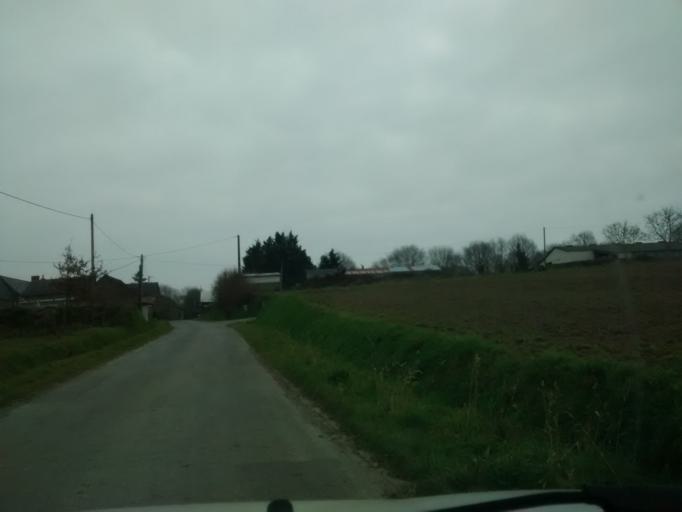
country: FR
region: Brittany
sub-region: Departement d'Ille-et-Vilaine
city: Bazouges-la-Perouse
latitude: 48.4045
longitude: -1.5586
